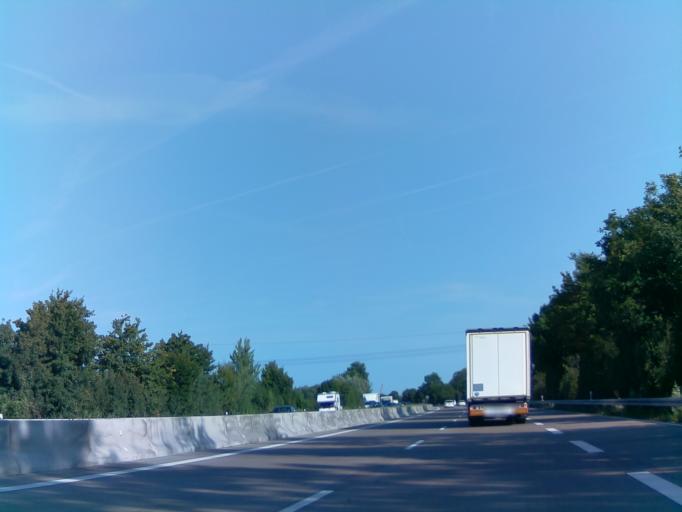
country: DE
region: Baden-Wuerttemberg
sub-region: Karlsruhe Region
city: Laudenbach
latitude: 49.6107
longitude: 8.6284
